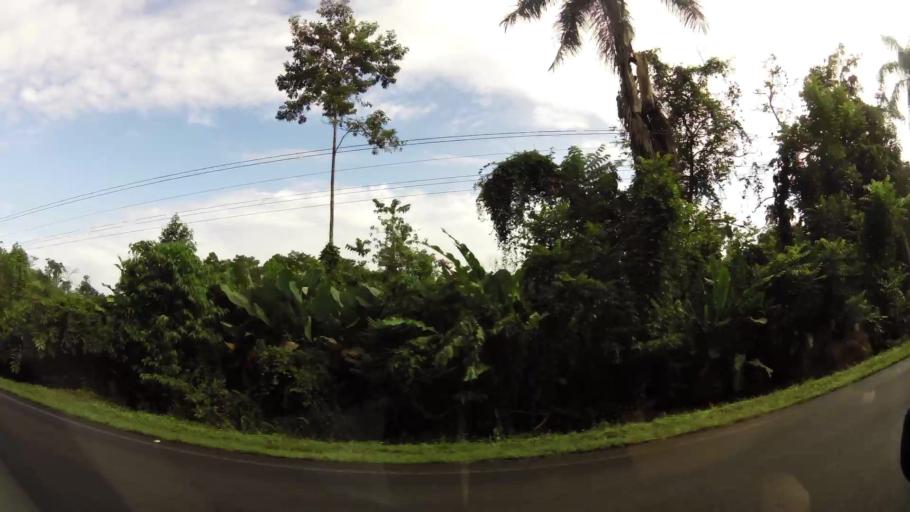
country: CR
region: Limon
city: Pocora
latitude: 10.1851
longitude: -83.6300
